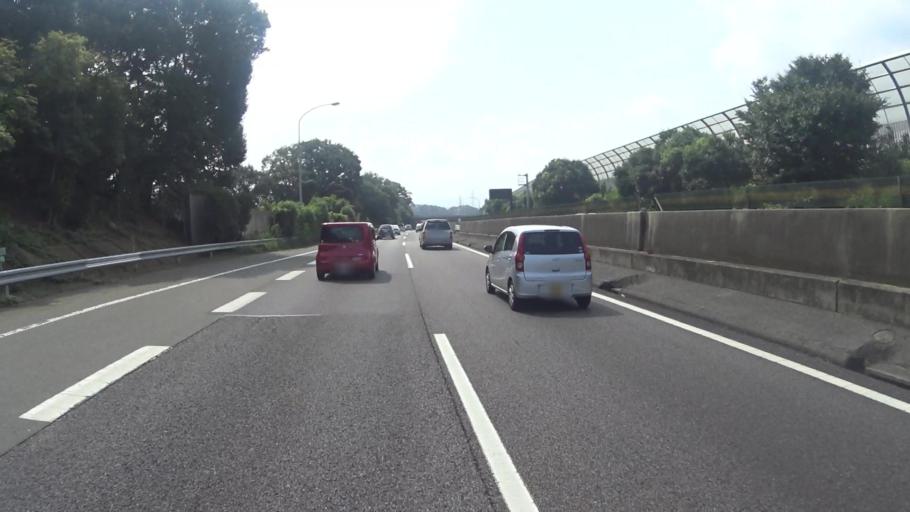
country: JP
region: Shiga Prefecture
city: Otsu-shi
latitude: 34.9950
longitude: 135.8728
